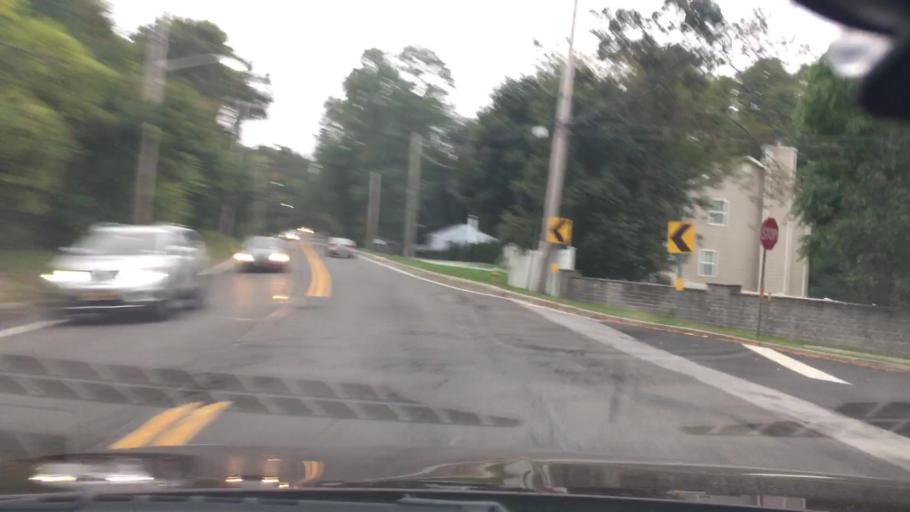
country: US
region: New York
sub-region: Suffolk County
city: Hauppauge
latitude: 40.8204
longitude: -73.2115
